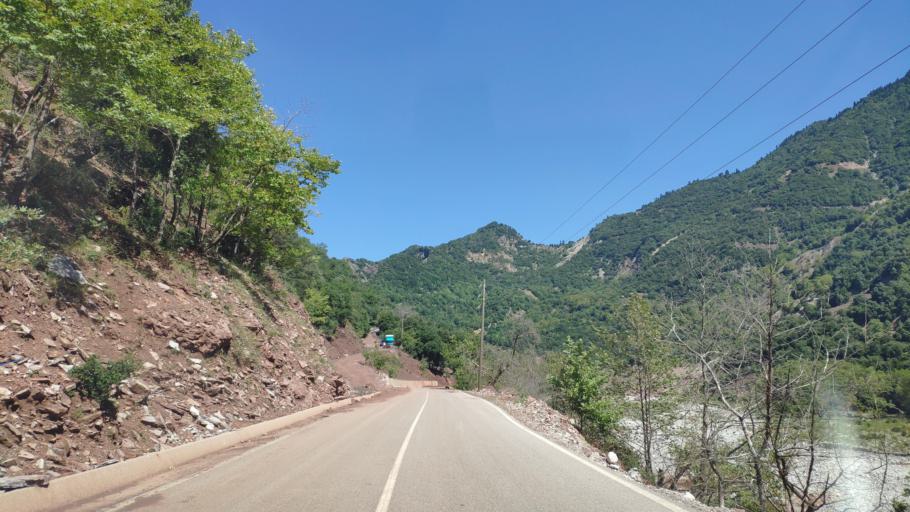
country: GR
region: Central Greece
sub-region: Nomos Evrytanias
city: Kerasochori
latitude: 39.0619
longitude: 21.6067
